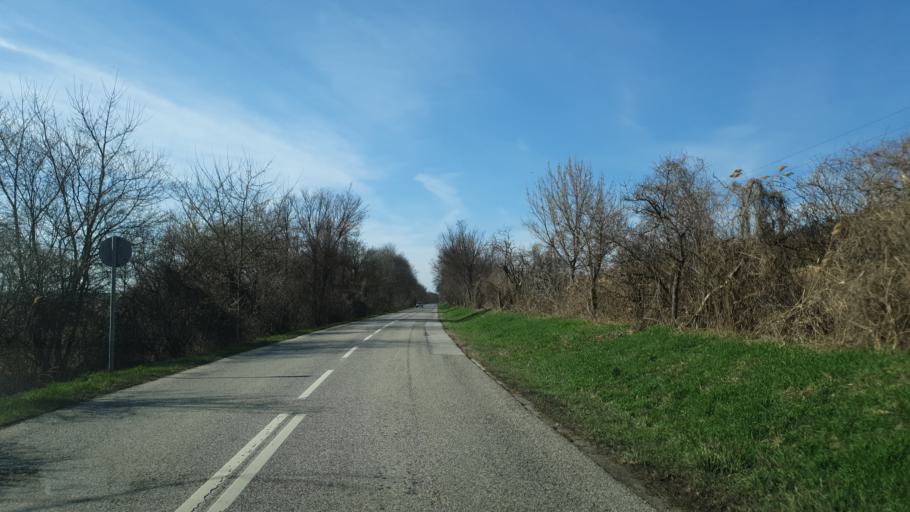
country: HU
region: Pest
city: Biatorbagy
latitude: 47.4814
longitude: 18.7805
